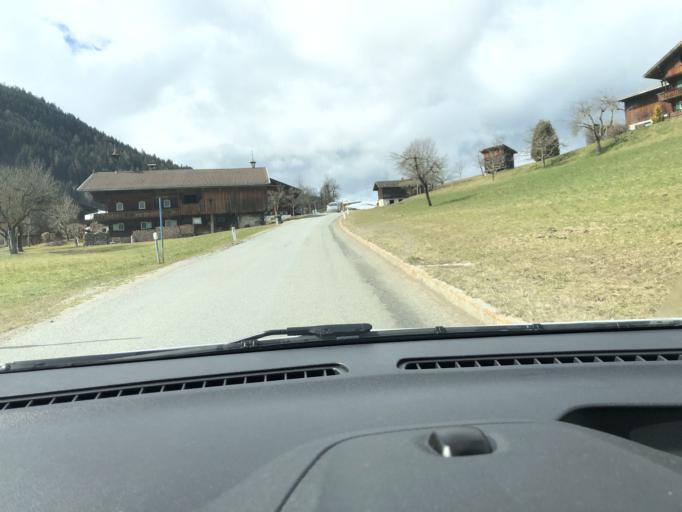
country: AT
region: Tyrol
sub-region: Politischer Bezirk Kitzbuhel
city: Itter
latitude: 47.4470
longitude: 12.1307
